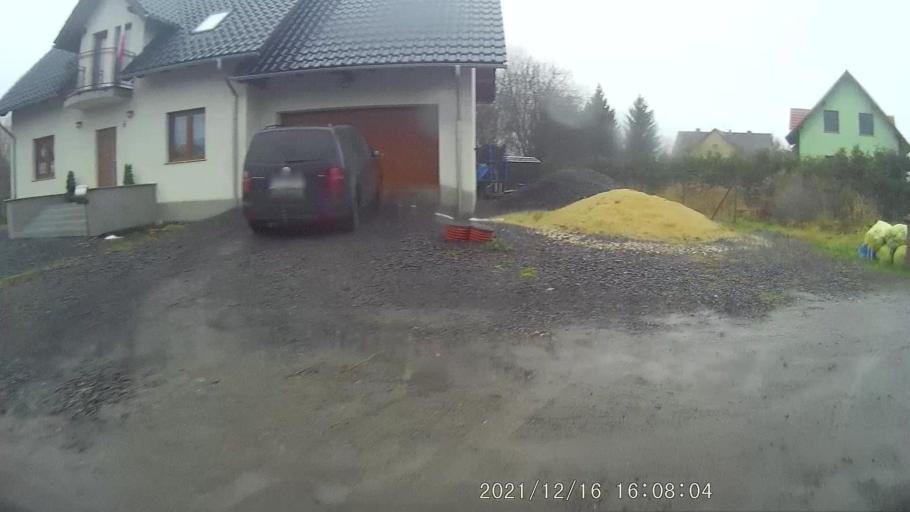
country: PL
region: Lower Silesian Voivodeship
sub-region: Powiat zgorzelecki
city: Lagow
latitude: 51.1583
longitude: 15.0498
